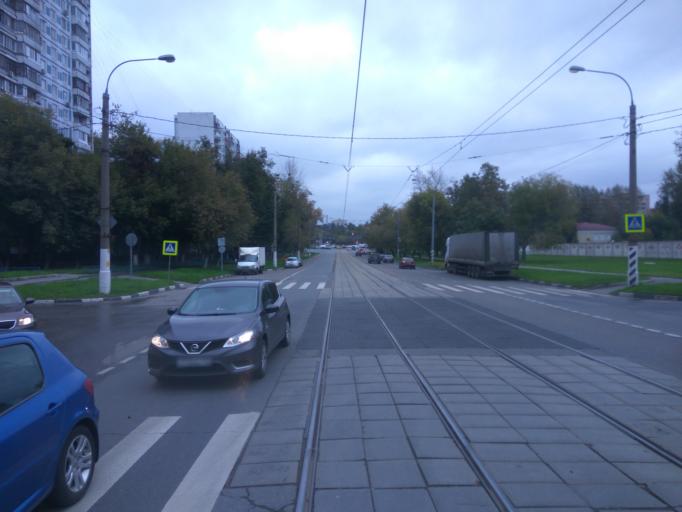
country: RU
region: Moscow
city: Kotlovka
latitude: 55.6609
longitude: 37.6103
